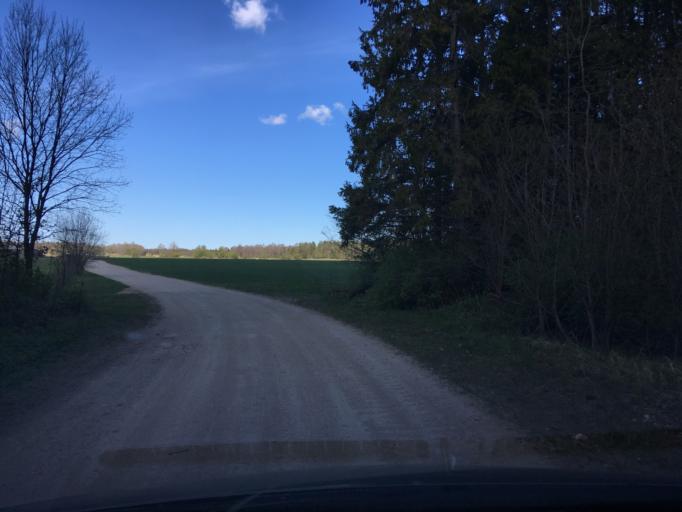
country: EE
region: Harju
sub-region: Raasiku vald
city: Raasiku
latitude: 59.2145
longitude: 25.1662
